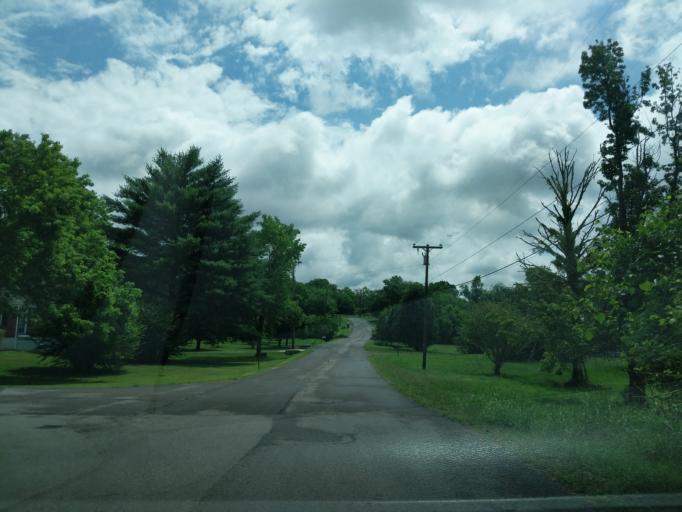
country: US
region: Tennessee
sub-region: Davidson County
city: Lakewood
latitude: 36.2363
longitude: -86.6743
